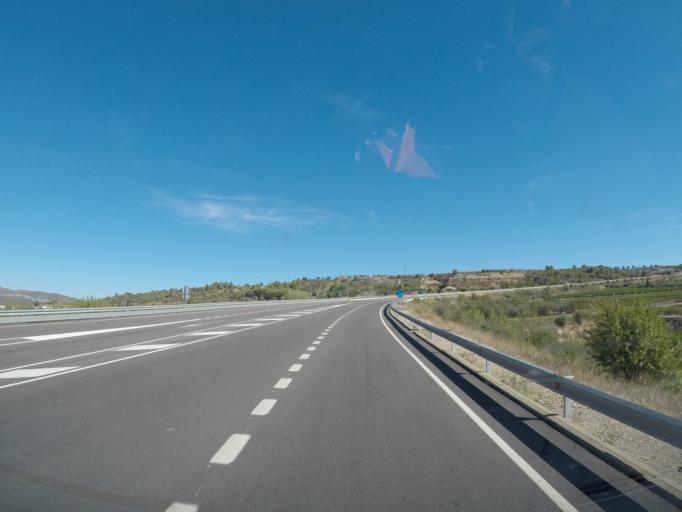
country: ES
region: Catalonia
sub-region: Provincia de Tarragona
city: Garcia
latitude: 41.1012
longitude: 0.6607
